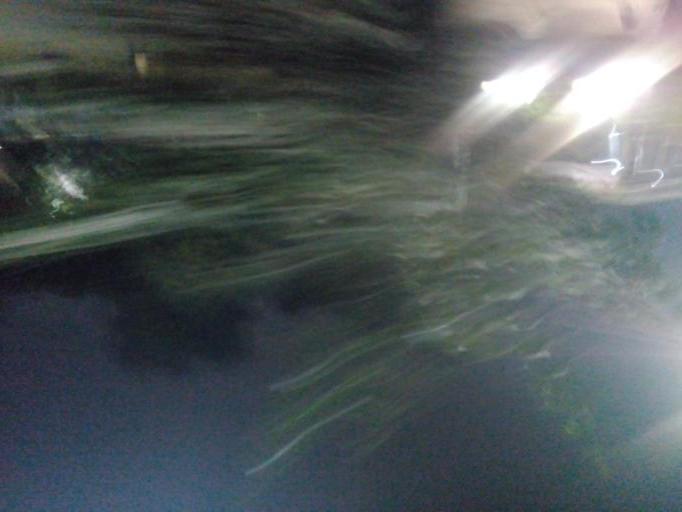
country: BD
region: Dhaka
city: Paltan
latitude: 23.7292
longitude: 90.4103
